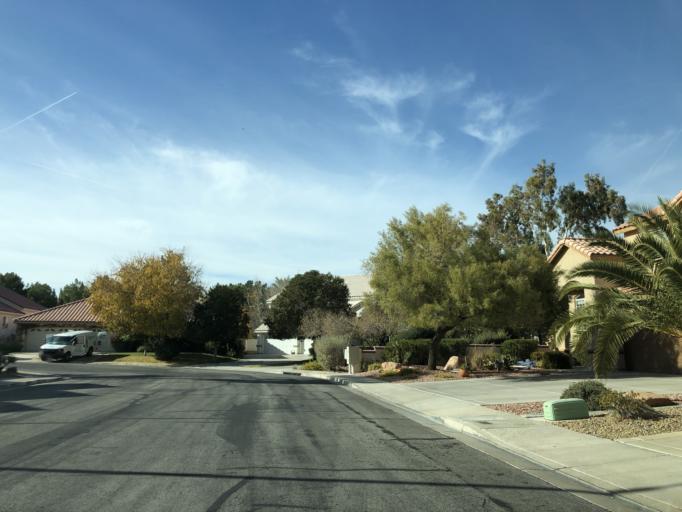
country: US
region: Nevada
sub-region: Clark County
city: Whitney
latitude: 36.0144
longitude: -115.0818
